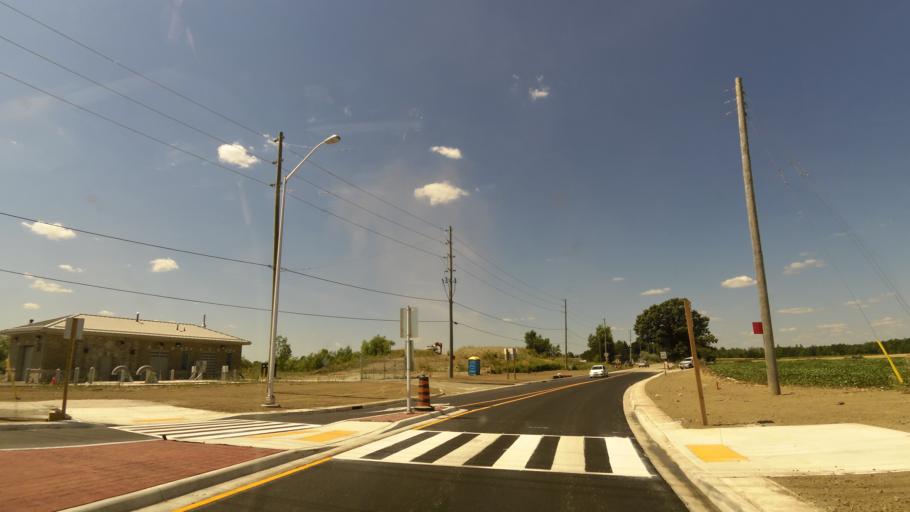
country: CA
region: Ontario
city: Brampton
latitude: 43.6381
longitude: -79.8627
